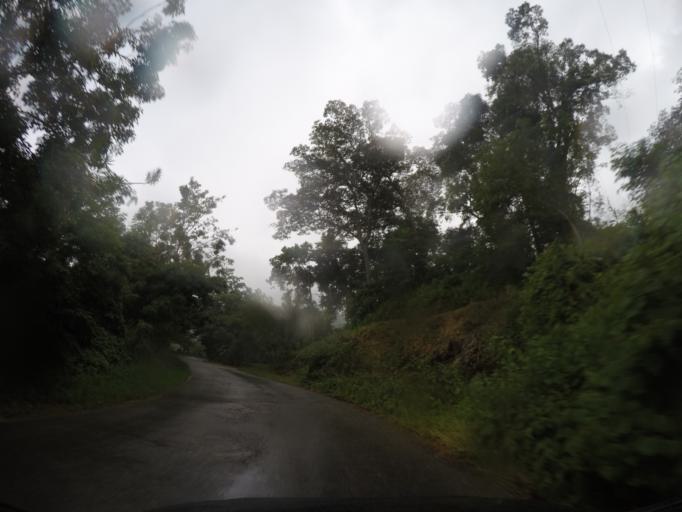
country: MX
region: Oaxaca
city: San Gabriel Mixtepec
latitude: 16.1074
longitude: -97.0651
